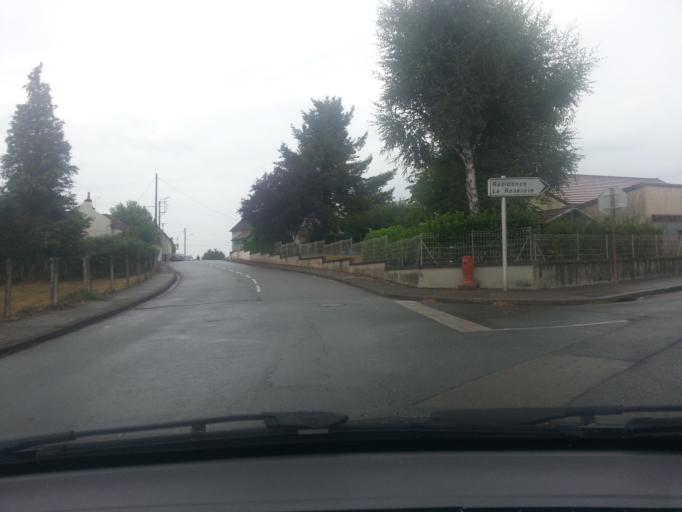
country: FR
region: Bourgogne
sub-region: Departement de Saone-et-Loire
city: Montchanin
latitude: 46.7430
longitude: 4.4672
